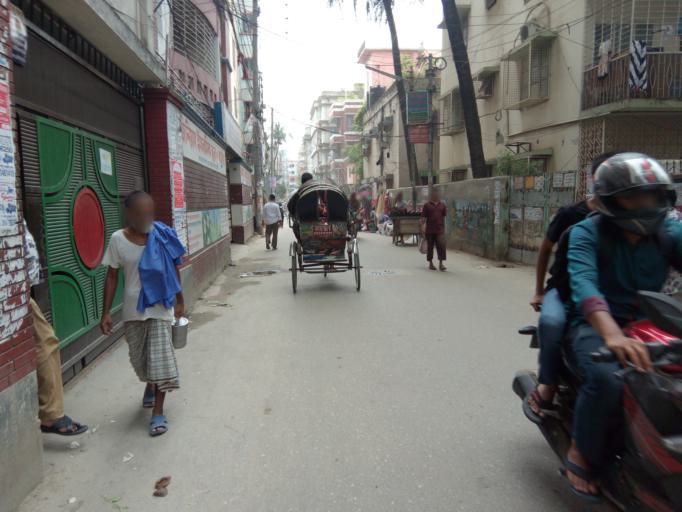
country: BD
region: Dhaka
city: Paltan
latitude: 23.7565
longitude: 90.4118
